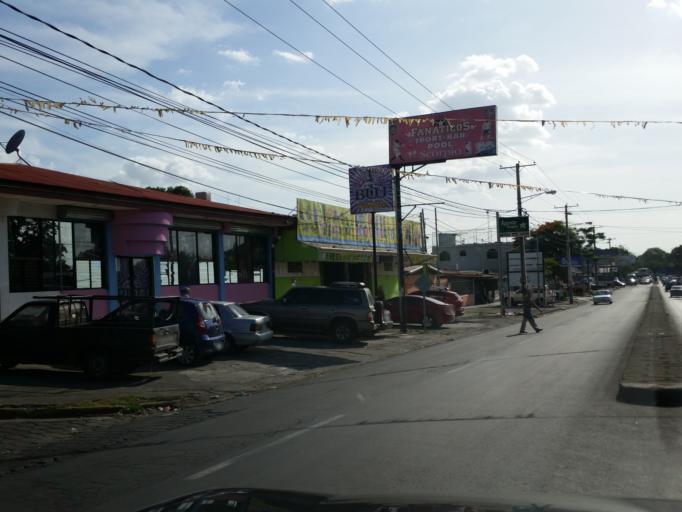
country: NI
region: Managua
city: Managua
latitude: 12.1462
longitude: -86.2358
